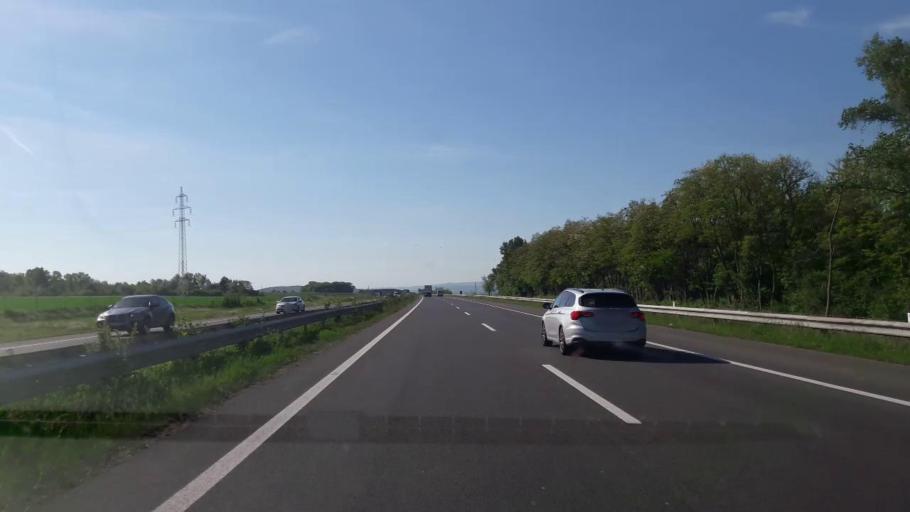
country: AT
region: Burgenland
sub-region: Eisenstadt-Umgebung
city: Steinbrunn
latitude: 47.8564
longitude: 16.4240
